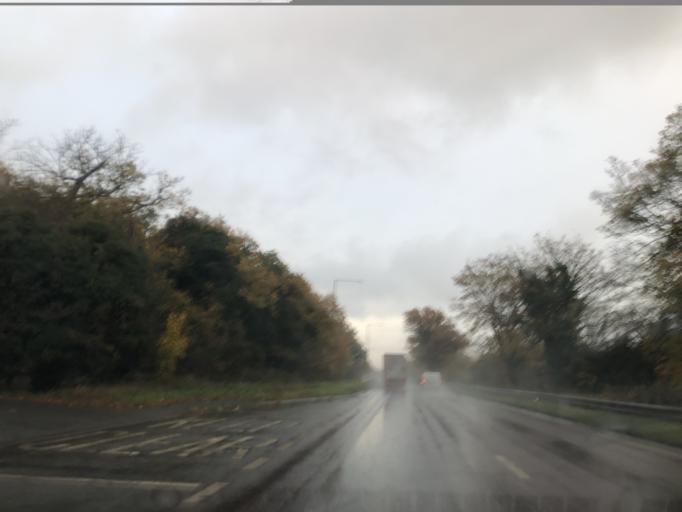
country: GB
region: England
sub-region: Solihull
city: Meriden
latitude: 52.4445
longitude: -1.6676
